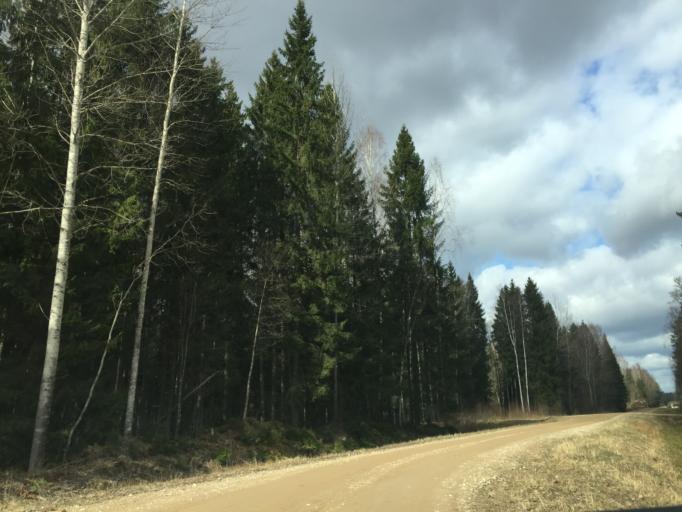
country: LV
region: Vecumnieki
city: Vecumnieki
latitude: 56.5893
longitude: 24.6420
